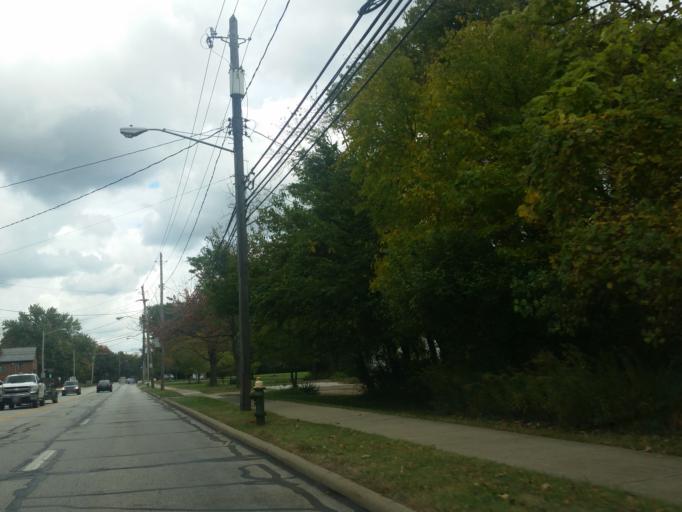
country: US
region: Ohio
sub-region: Cuyahoga County
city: Westlake
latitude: 41.4450
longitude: -81.9315
